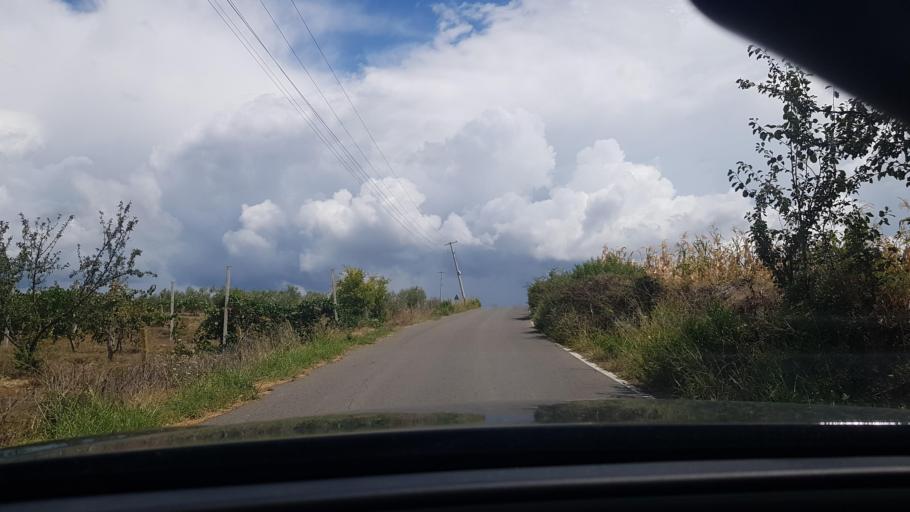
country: AL
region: Durres
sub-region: Rrethi i Durresit
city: Rrashbull
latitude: 41.2957
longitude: 19.5291
